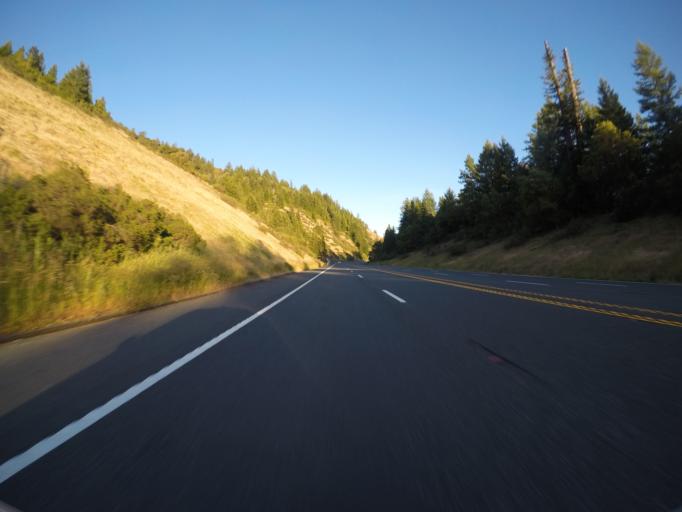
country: US
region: California
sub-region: Mendocino County
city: Laytonville
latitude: 39.8323
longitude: -123.6770
